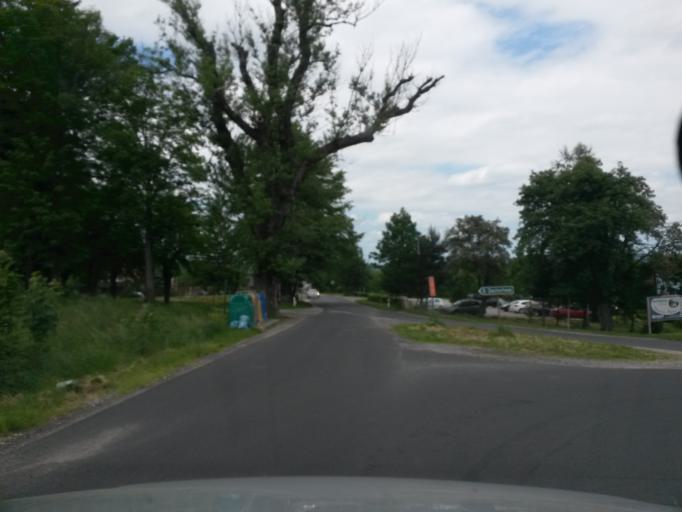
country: PL
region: Lower Silesian Voivodeship
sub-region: Powiat jeleniogorski
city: Podgorzyn
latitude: 50.8356
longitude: 15.6630
